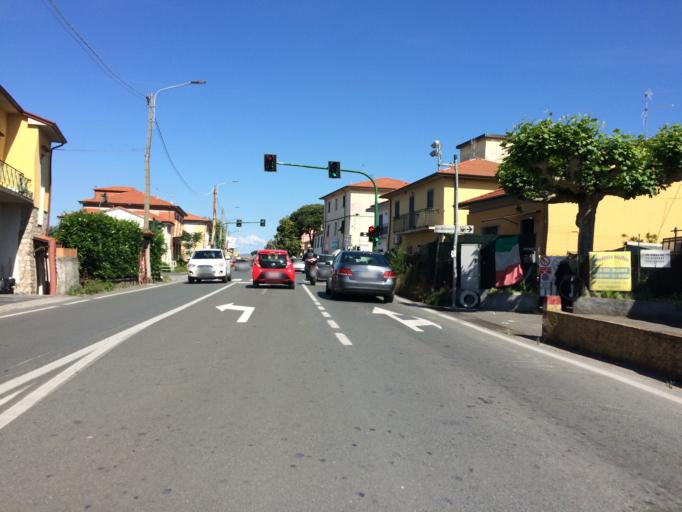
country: IT
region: Liguria
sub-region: Provincia di La Spezia
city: Casano-Dogana-Isola
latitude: 44.0658
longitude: 10.0322
